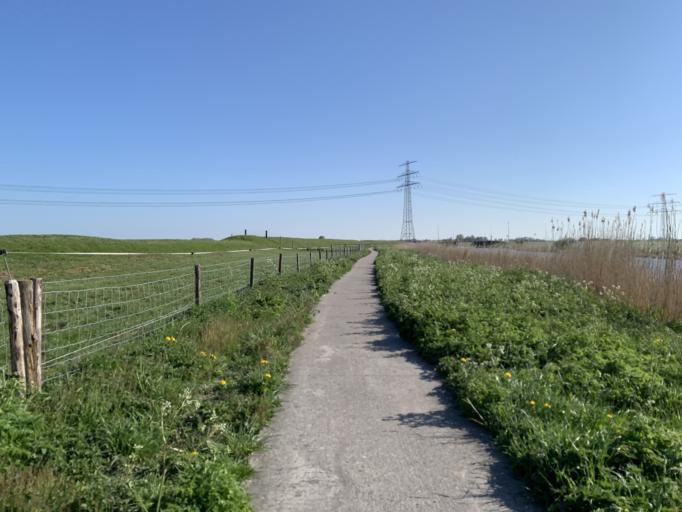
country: NL
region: Groningen
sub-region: Gemeente Winsum
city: Winsum
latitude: 53.2952
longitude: 6.5050
